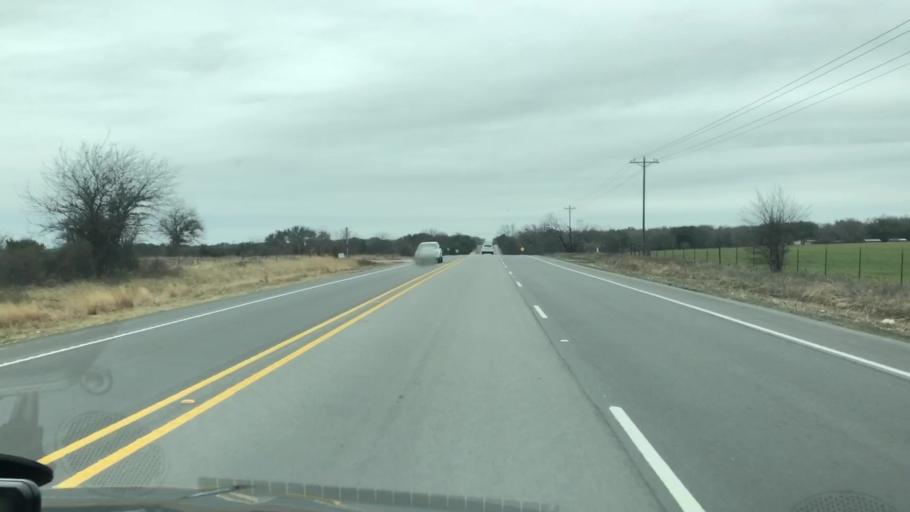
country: US
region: Texas
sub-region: Erath County
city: Stephenville
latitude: 32.1589
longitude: -98.1482
